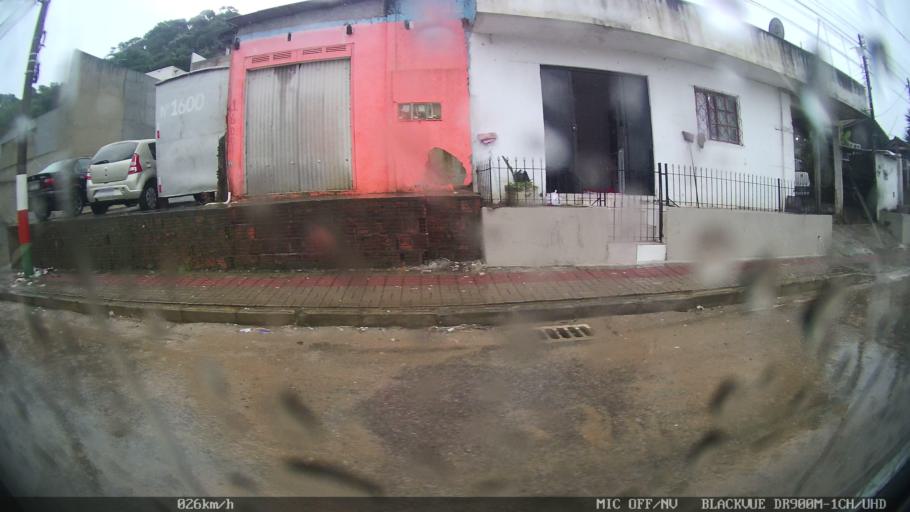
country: BR
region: Santa Catarina
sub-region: Balneario Camboriu
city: Balneario Camboriu
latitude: -27.0071
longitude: -48.6482
